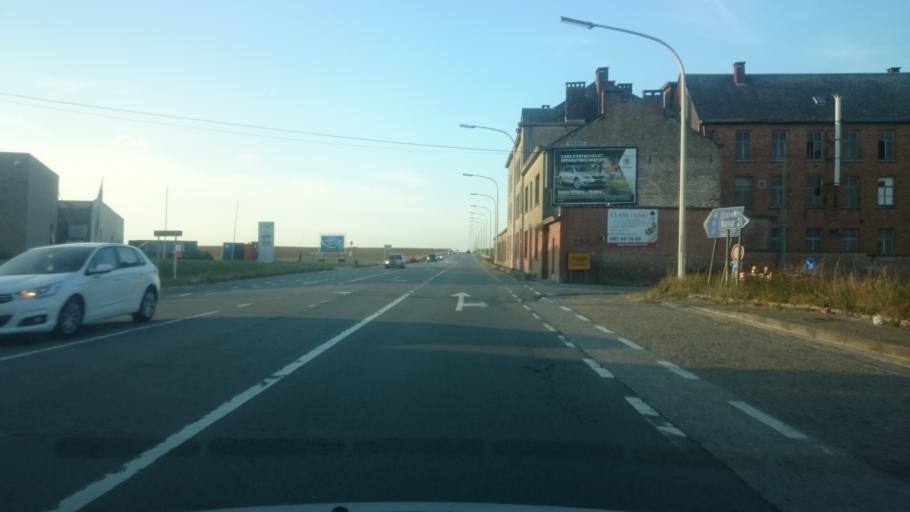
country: BE
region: Wallonia
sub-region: Province de Namur
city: Gembloux
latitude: 50.5798
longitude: 4.6867
